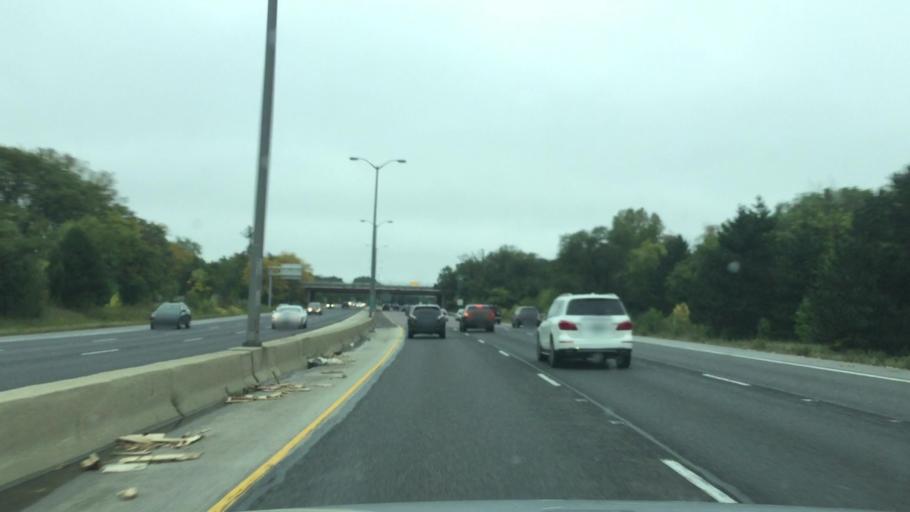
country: US
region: Illinois
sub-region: Cook County
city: Glenview
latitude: 42.0707
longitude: -87.7579
